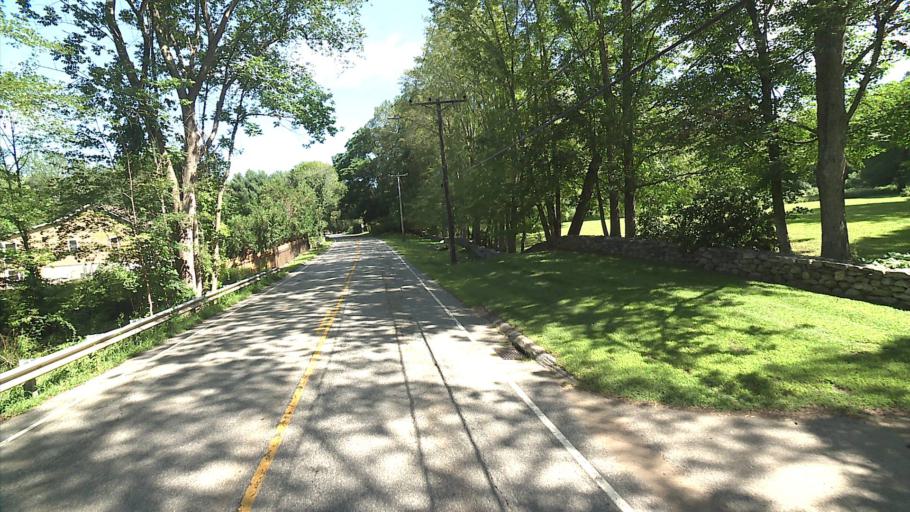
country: US
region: Connecticut
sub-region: Windham County
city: Windham
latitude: 41.6945
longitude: -72.0827
